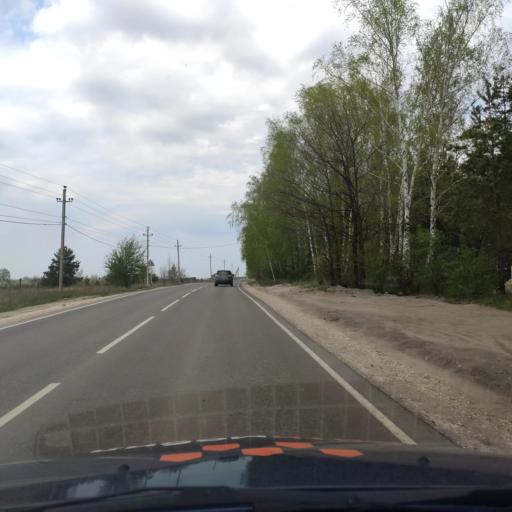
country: RU
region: Voronezj
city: Podgornoye
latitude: 51.8400
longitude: 39.1434
